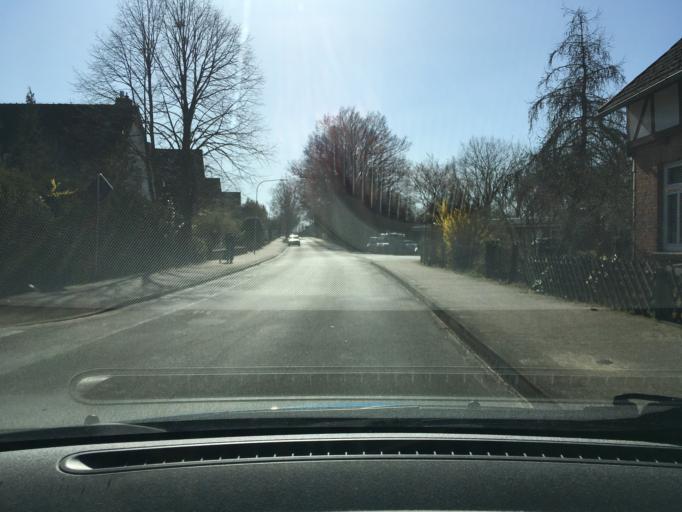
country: DE
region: Lower Saxony
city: Ebstorf
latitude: 53.0249
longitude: 10.4098
